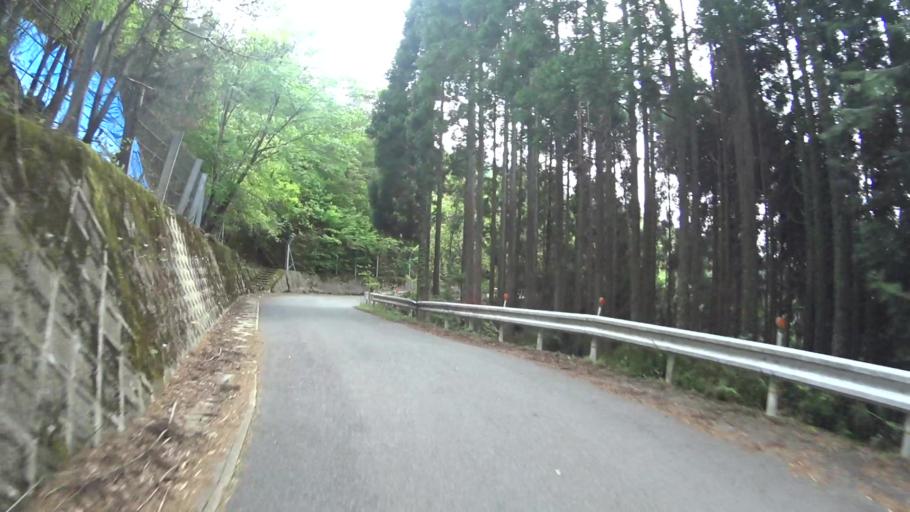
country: JP
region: Kyoto
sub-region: Kyoto-shi
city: Kamigyo-ku
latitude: 35.1154
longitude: 135.7082
